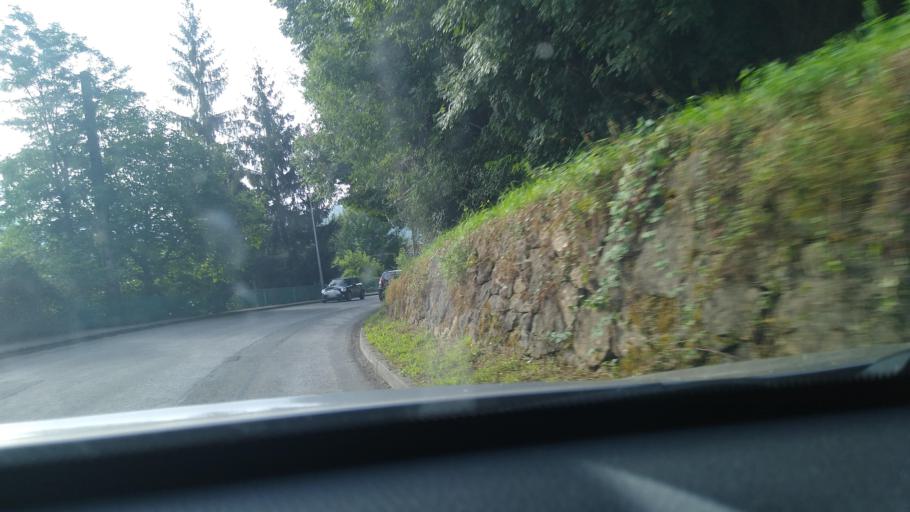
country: FR
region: Midi-Pyrenees
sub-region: Departement de l'Ariege
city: Saint-Girons
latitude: 42.9775
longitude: 1.1478
